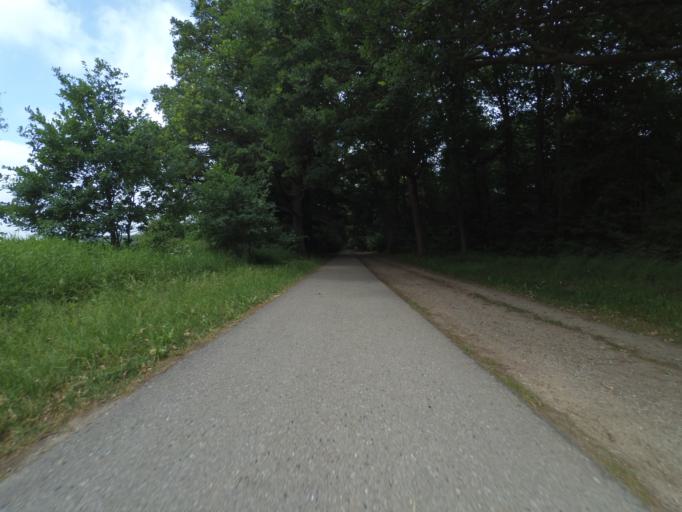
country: DE
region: Mecklenburg-Vorpommern
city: Malchow
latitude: 53.4870
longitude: 12.5079
